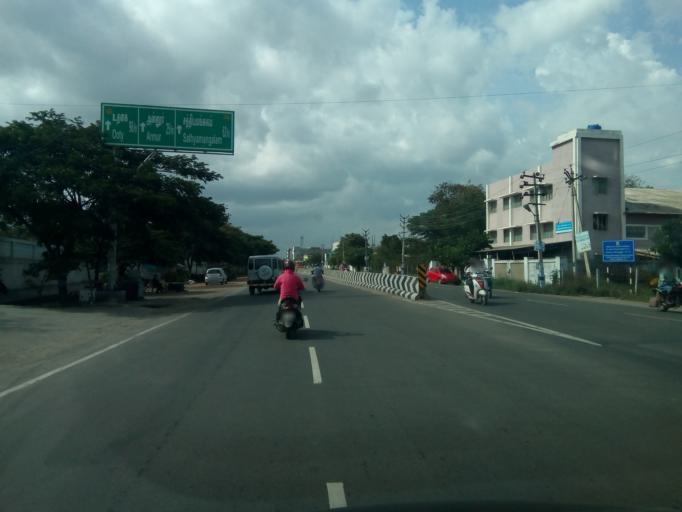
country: IN
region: Tamil Nadu
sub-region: Coimbatore
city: Irugur
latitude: 11.0400
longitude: 77.0376
